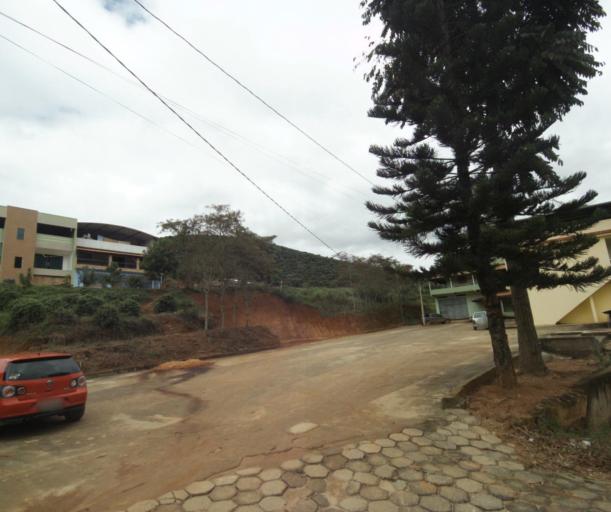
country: BR
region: Espirito Santo
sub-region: Irupi
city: Irupi
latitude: -20.3489
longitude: -41.6387
